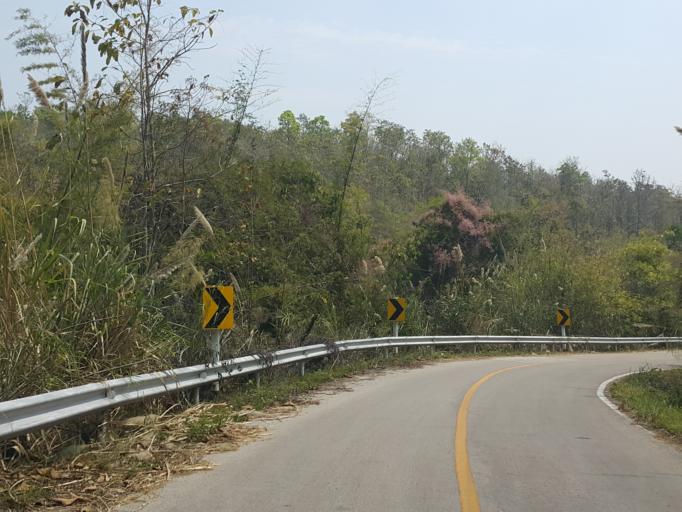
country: TH
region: Lampang
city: Mueang Pan
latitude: 18.8010
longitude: 99.4871
